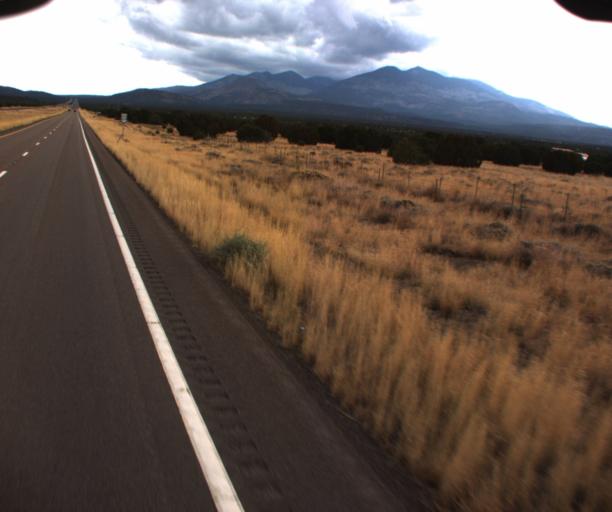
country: US
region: Arizona
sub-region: Coconino County
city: Flagstaff
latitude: 35.4393
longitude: -111.5662
